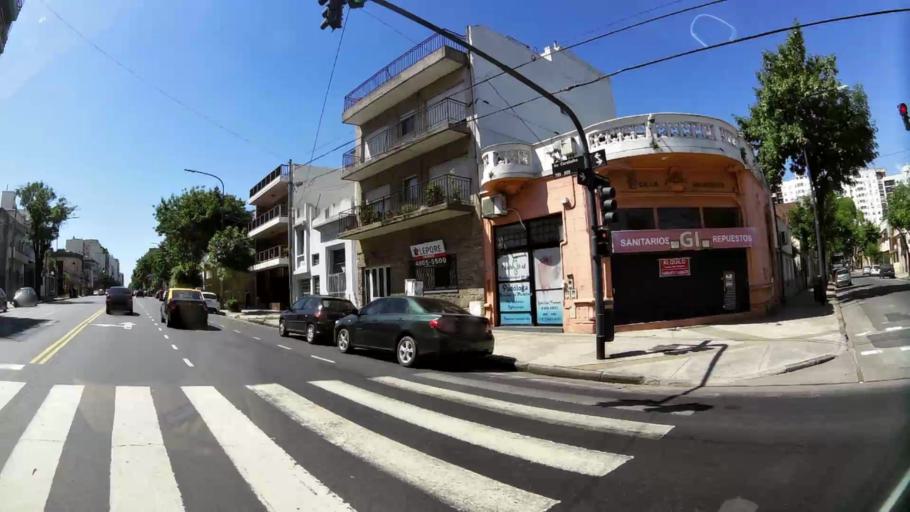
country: AR
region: Buenos Aires F.D.
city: Villa Santa Rita
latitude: -34.6355
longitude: -58.4523
